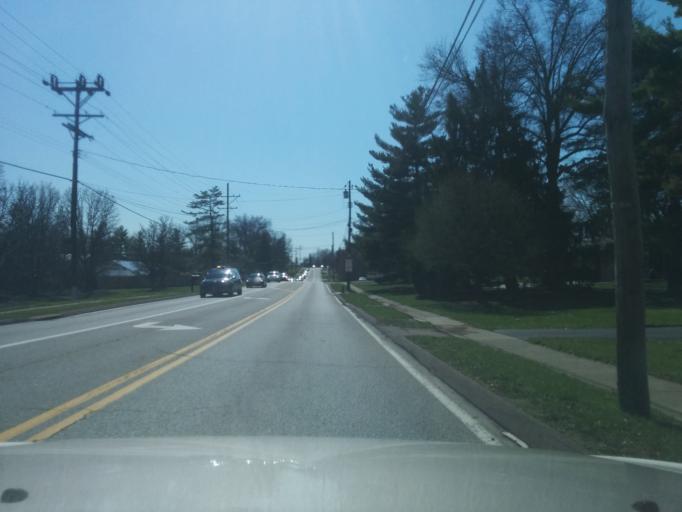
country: US
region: Ohio
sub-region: Hamilton County
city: Groesbeck
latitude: 39.2314
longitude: -84.5992
